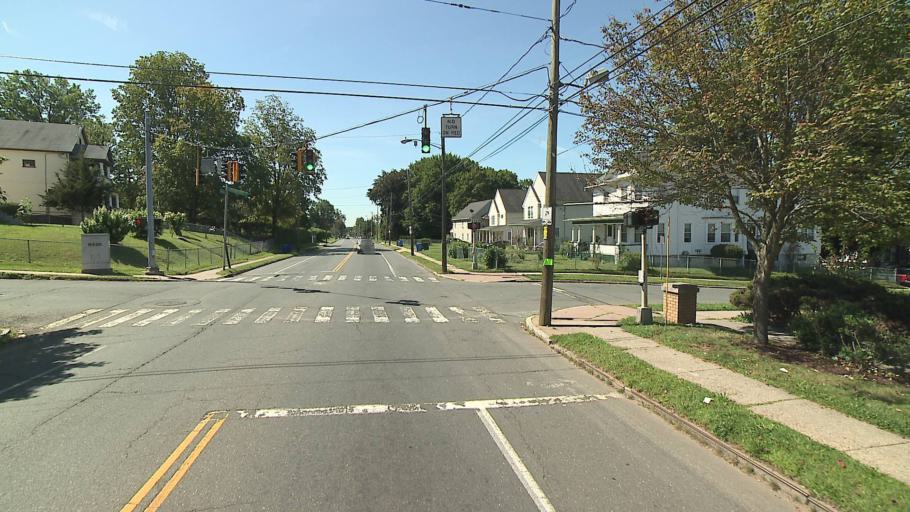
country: US
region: Connecticut
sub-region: Hartford County
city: Blue Hills
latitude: 41.7986
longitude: -72.6956
